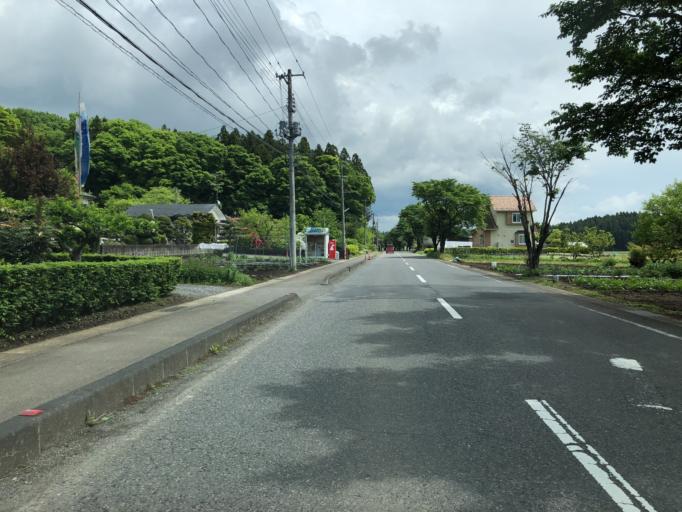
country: JP
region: Fukushima
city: Ishikawa
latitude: 37.1125
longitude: 140.3282
